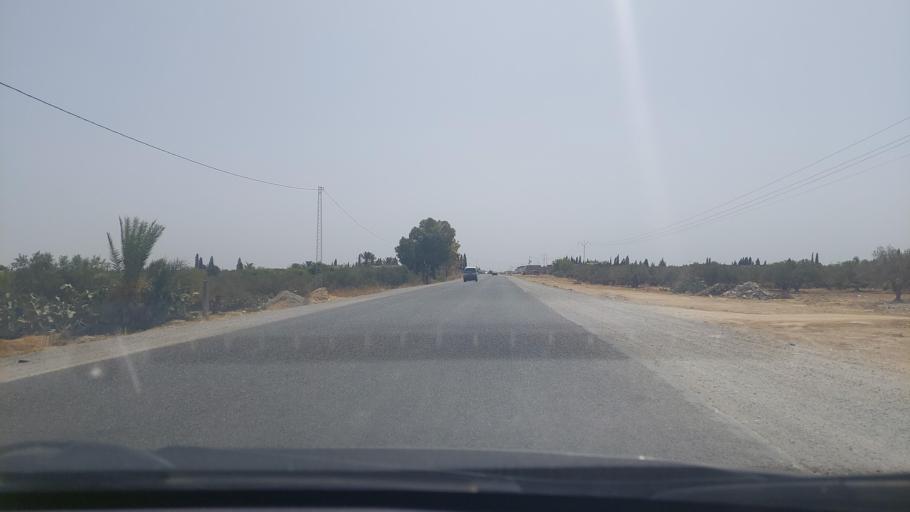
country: TN
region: Al Munastir
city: Qasr Hallal
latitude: 35.6261
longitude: 10.8724
